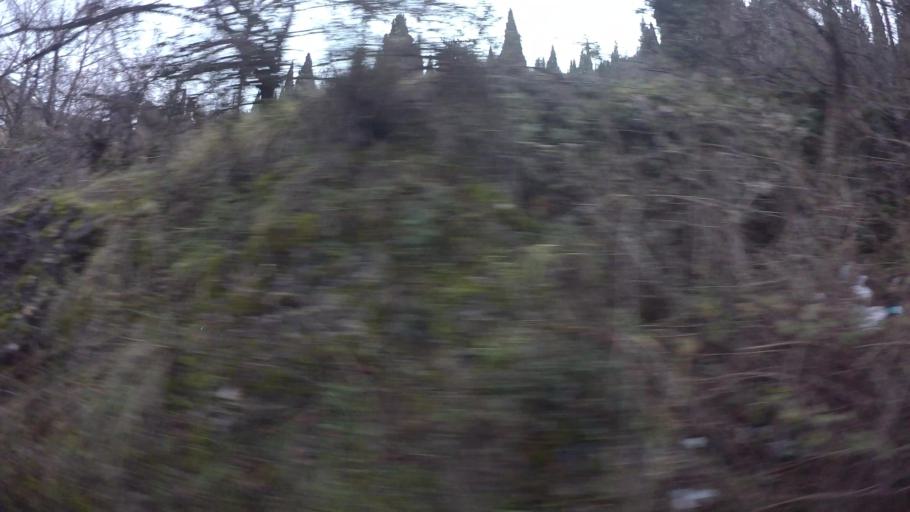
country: BA
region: Federation of Bosnia and Herzegovina
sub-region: Hercegovacko-Bosanski Kanton
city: Mostar
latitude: 43.3338
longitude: 17.8006
